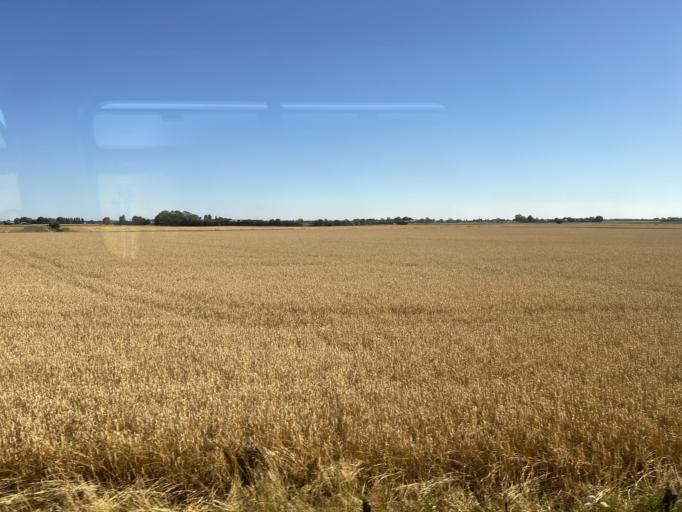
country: GB
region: England
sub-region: Lincolnshire
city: Spilsby
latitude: 53.1320
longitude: 0.1515
